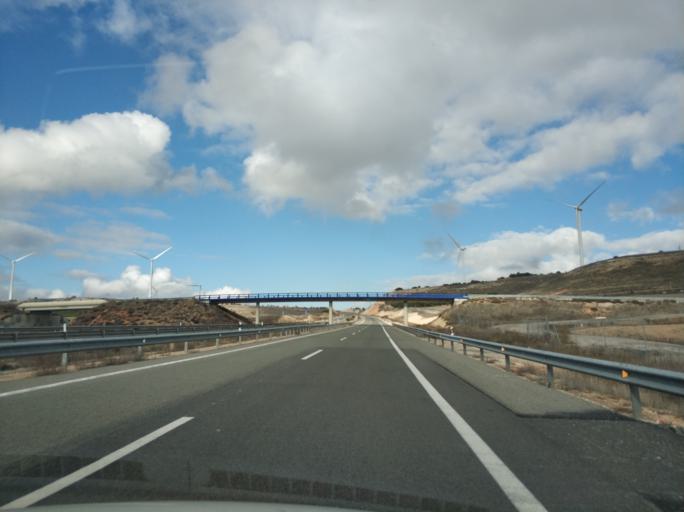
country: ES
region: Castille and Leon
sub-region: Provincia de Soria
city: Alcubilla de las Penas
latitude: 41.2840
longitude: -2.4759
